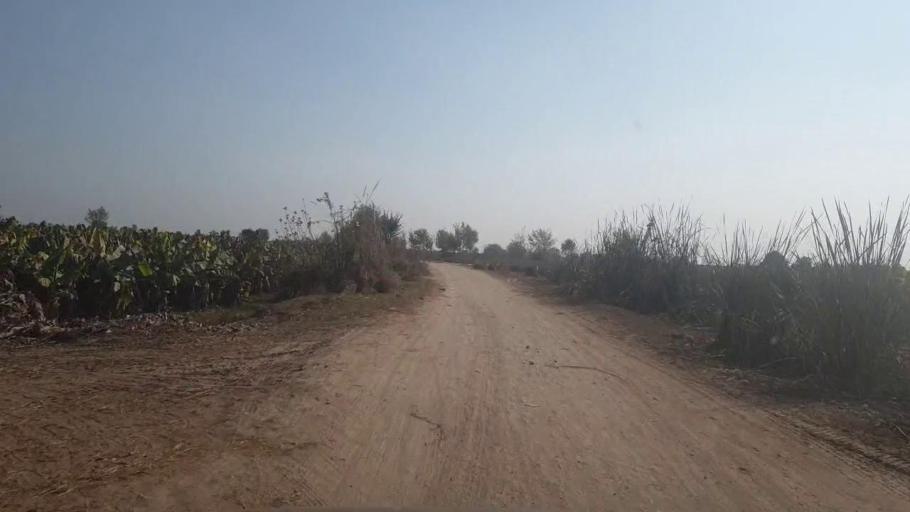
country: PK
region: Sindh
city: Sakrand
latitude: 26.0712
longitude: 68.4288
